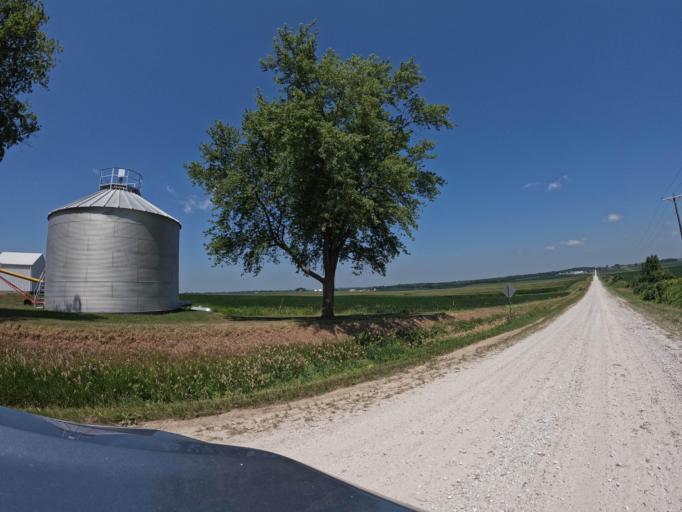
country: US
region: Iowa
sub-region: Keokuk County
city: Sigourney
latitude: 41.2819
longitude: -92.2189
